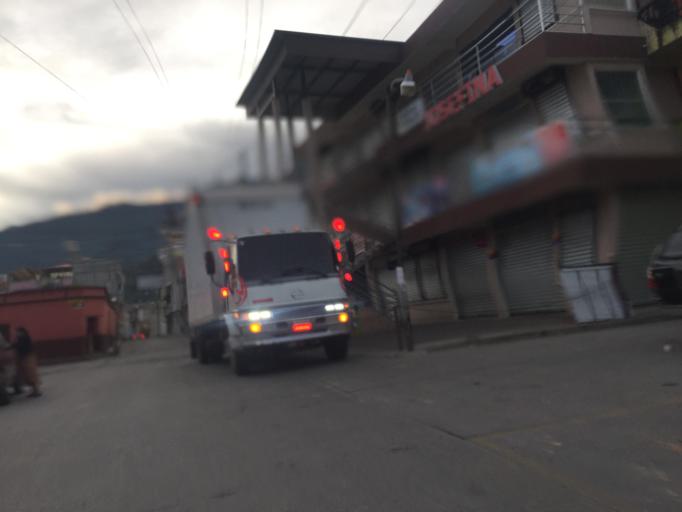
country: GT
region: Totonicapan
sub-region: Municipio de Totonicapan
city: Totonicapan
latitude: 14.9092
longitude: -91.3608
